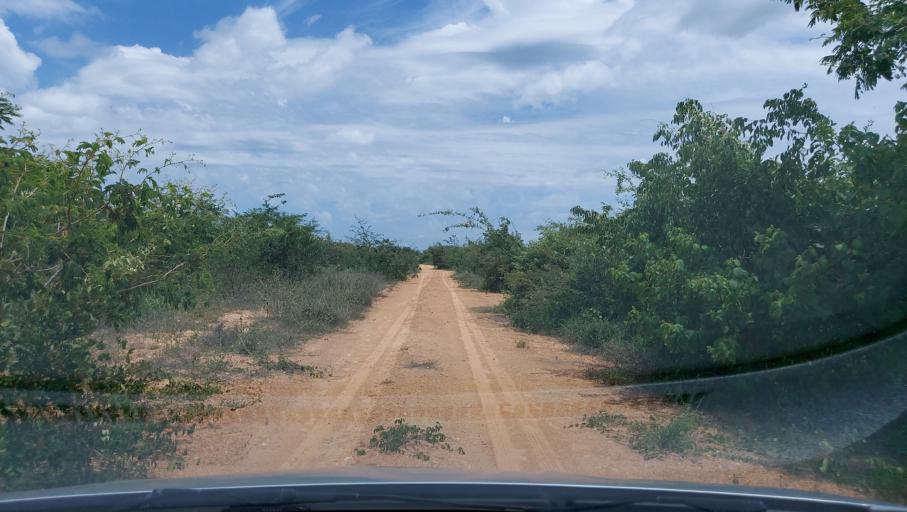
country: BR
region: Bahia
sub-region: Oliveira Dos Brejinhos
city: Beira Rio
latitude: -12.0122
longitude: -42.6310
